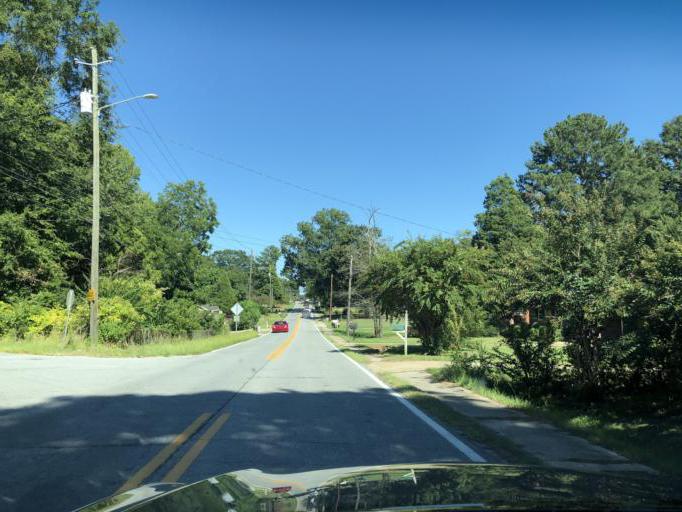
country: US
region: Georgia
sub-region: Muscogee County
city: Columbus
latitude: 32.5069
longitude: -84.9303
